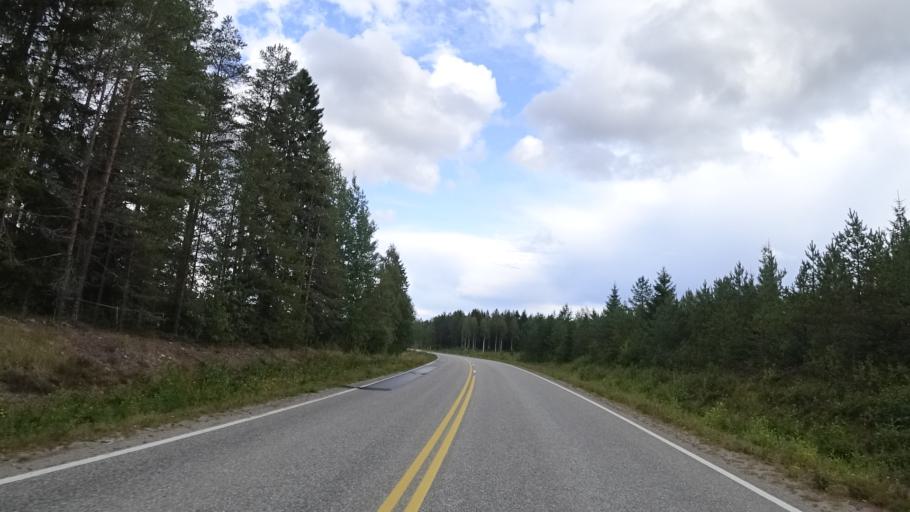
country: FI
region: North Karelia
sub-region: Joensuu
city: Ilomantsi
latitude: 62.6481
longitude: 30.9967
